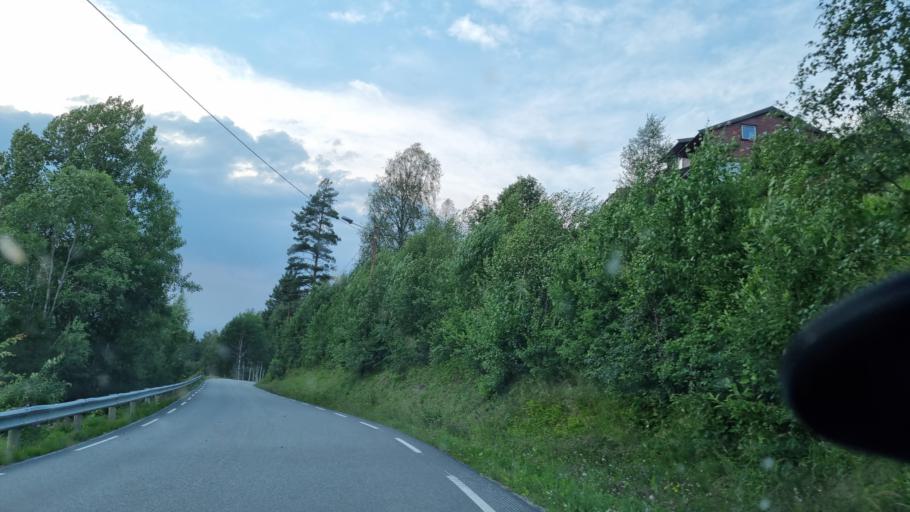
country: NO
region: Hedmark
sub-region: Trysil
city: Innbygda
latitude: 61.3209
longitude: 12.2596
